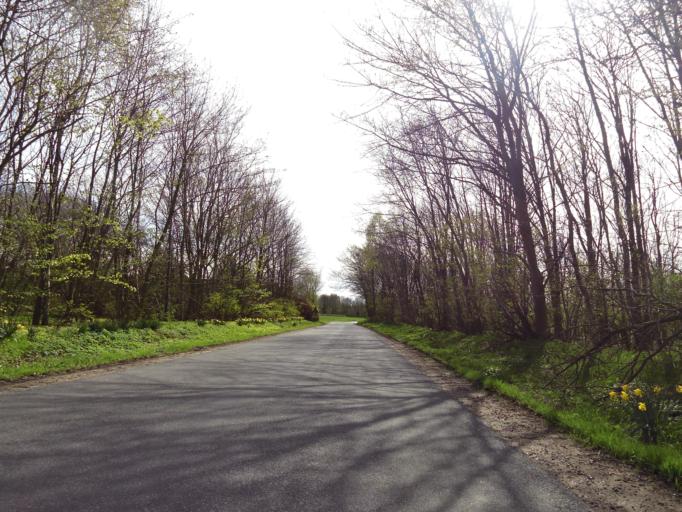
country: DK
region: Central Jutland
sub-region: Skive Kommune
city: Skive
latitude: 56.5441
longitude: 8.9552
